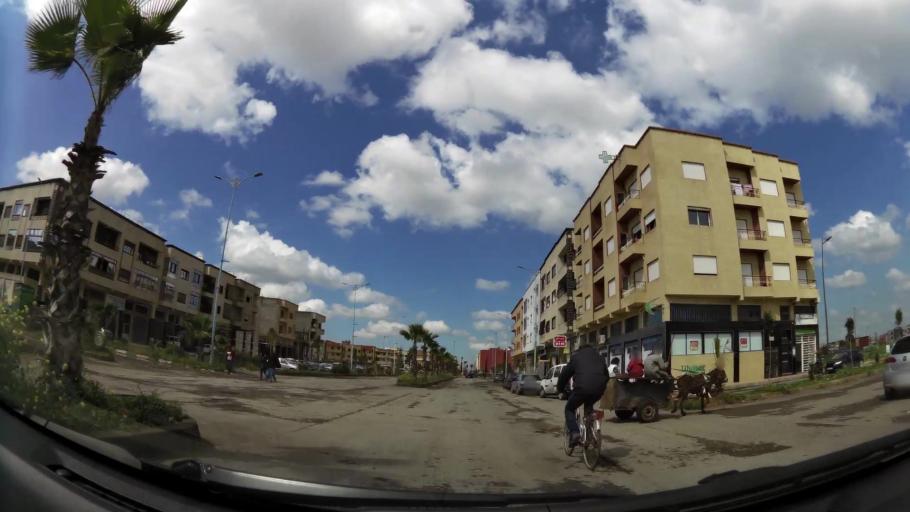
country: MA
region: Grand Casablanca
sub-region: Mediouna
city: Mediouna
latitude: 33.3805
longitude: -7.5348
